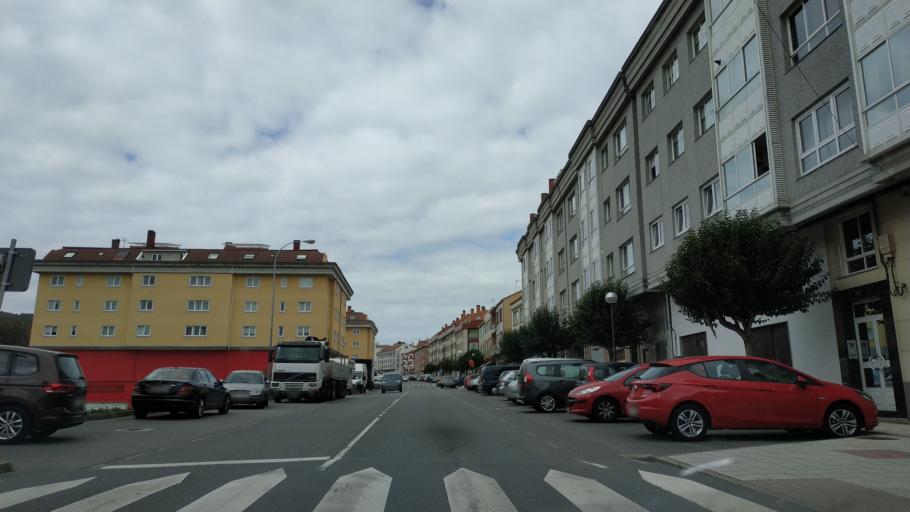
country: ES
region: Galicia
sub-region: Provincia da Coruna
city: Arteixo
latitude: 43.3016
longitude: -8.5119
